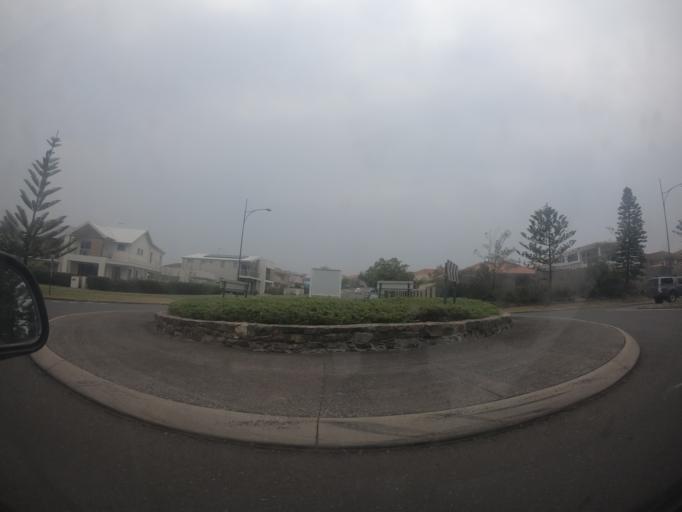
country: AU
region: New South Wales
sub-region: Shellharbour
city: Flinders
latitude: -34.5907
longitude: 150.8581
